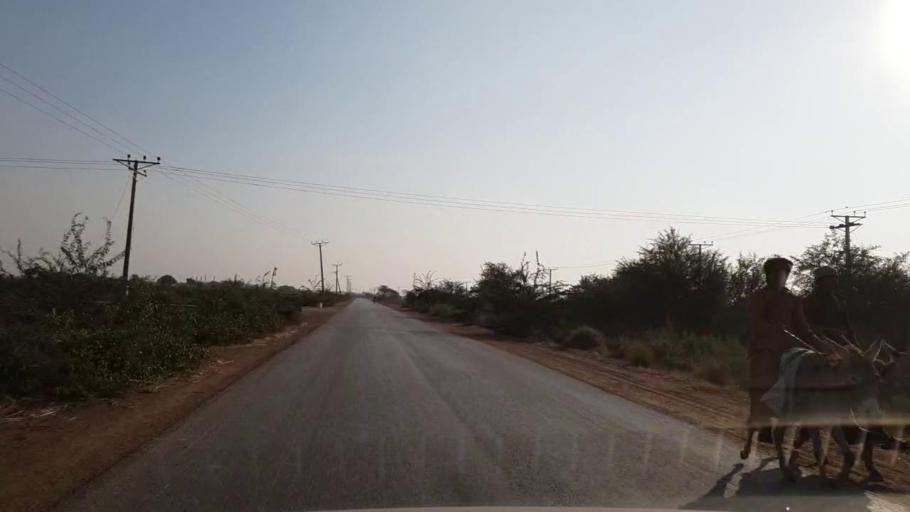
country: PK
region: Sindh
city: Bulri
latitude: 24.8239
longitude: 68.3224
